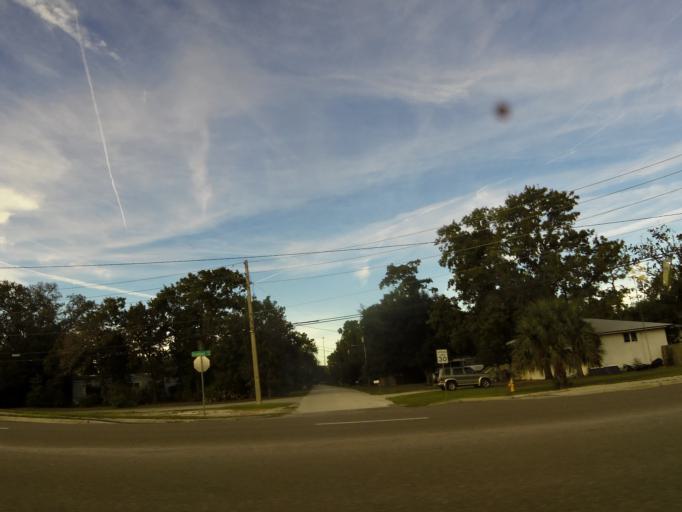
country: US
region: Florida
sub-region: Saint Johns County
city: Fruit Cove
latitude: 30.1618
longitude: -81.5500
